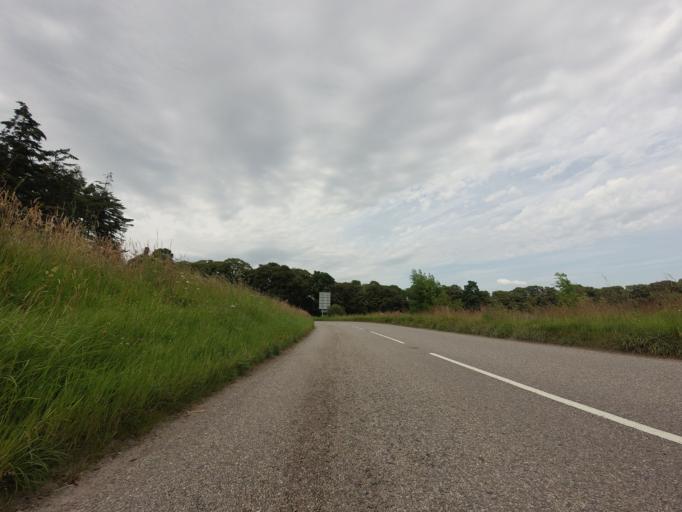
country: GB
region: Scotland
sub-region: Highland
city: Alness
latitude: 57.8542
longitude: -4.3049
